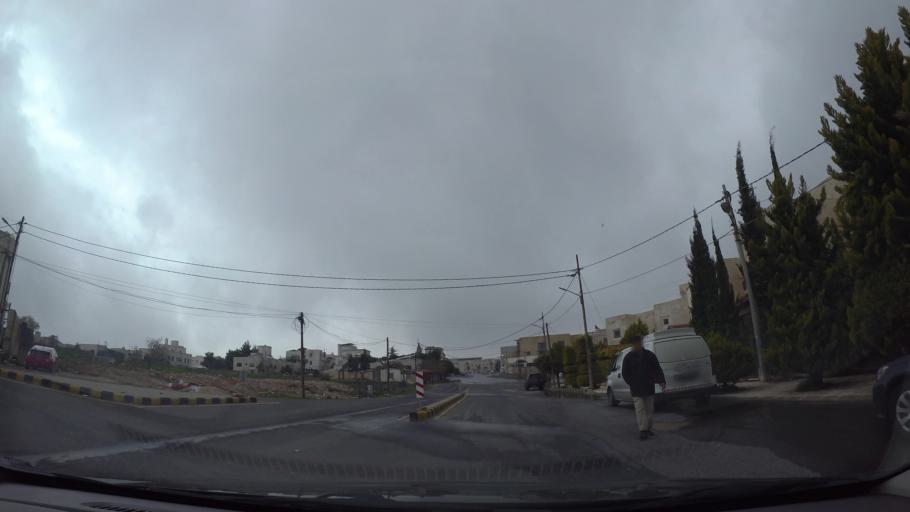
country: JO
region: Amman
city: Al Bunayyat ash Shamaliyah
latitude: 31.9440
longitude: 35.8850
